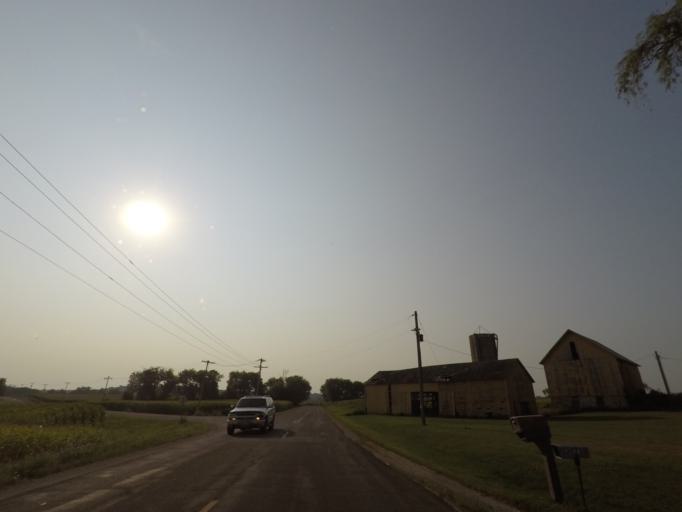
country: US
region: Wisconsin
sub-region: Dane County
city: Cottage Grove
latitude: 43.0493
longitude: -89.2419
